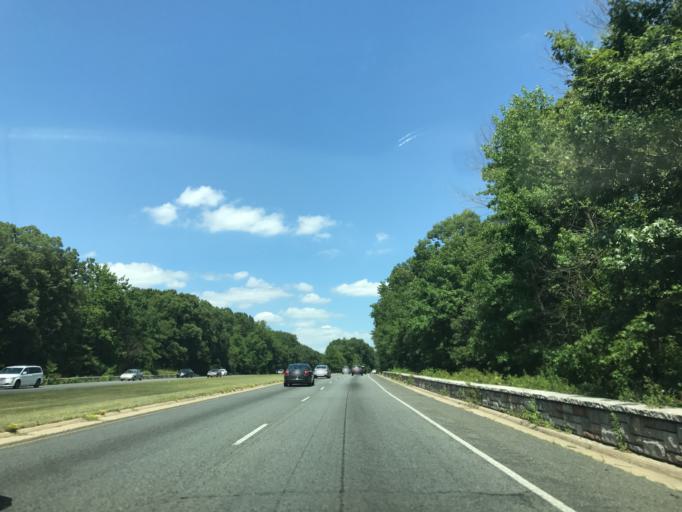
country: US
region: Maryland
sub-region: Anne Arundel County
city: Maryland City
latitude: 39.0778
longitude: -76.8235
